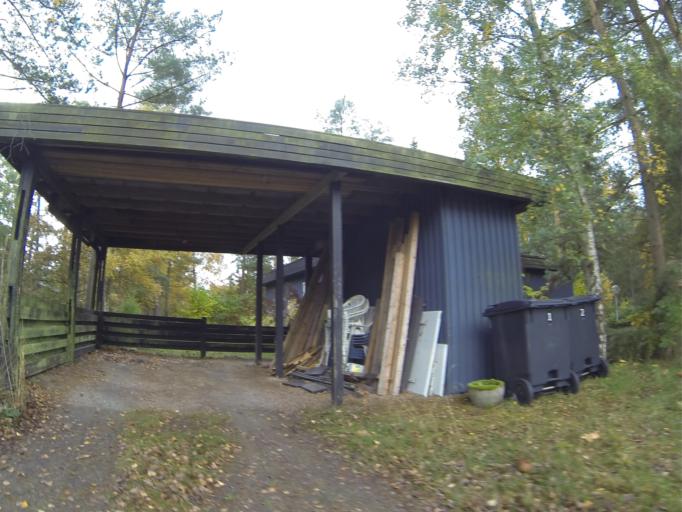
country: SE
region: Skane
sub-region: Sjobo Kommun
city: Sjoebo
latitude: 55.6327
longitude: 13.6438
